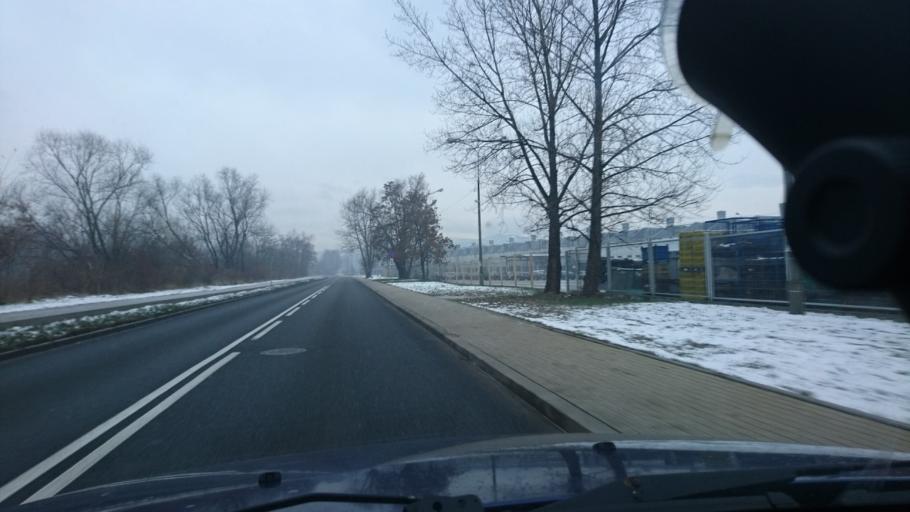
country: PL
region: Silesian Voivodeship
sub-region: Bielsko-Biala
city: Bielsko-Biala
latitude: 49.8455
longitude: 19.0469
